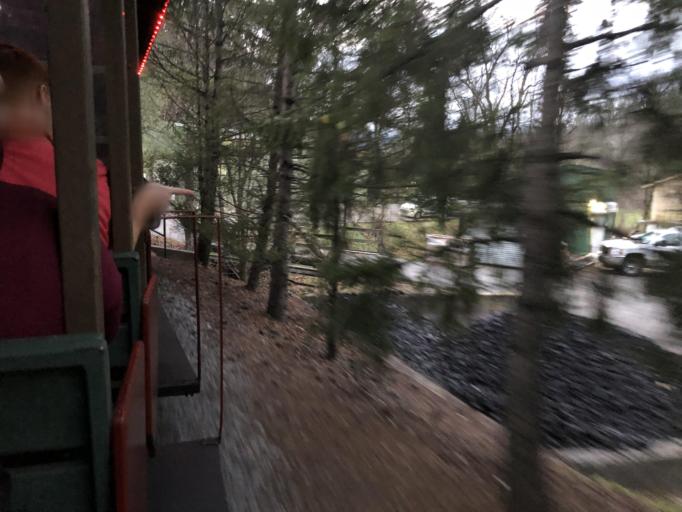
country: US
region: Tennessee
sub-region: Sevier County
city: Pigeon Forge
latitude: 35.7914
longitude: -83.5361
